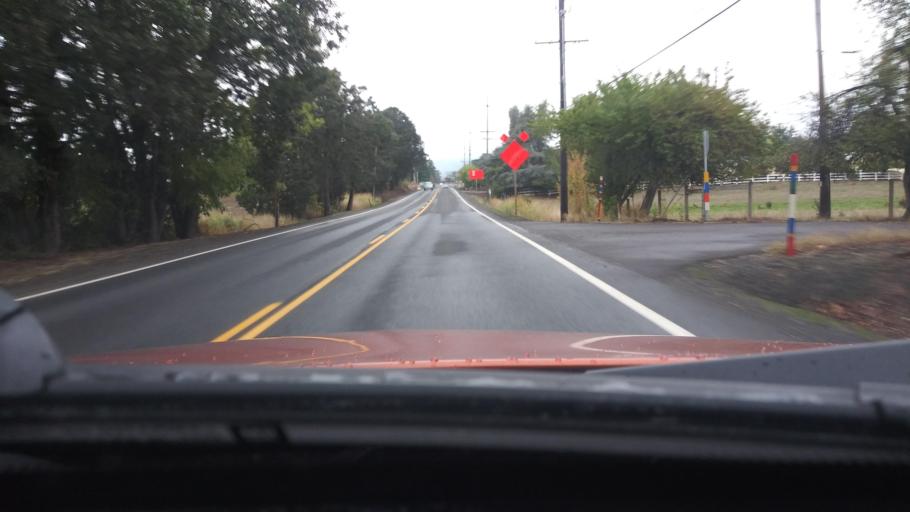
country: US
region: Oregon
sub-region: Washington County
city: Banks
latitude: 45.6049
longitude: -123.1145
